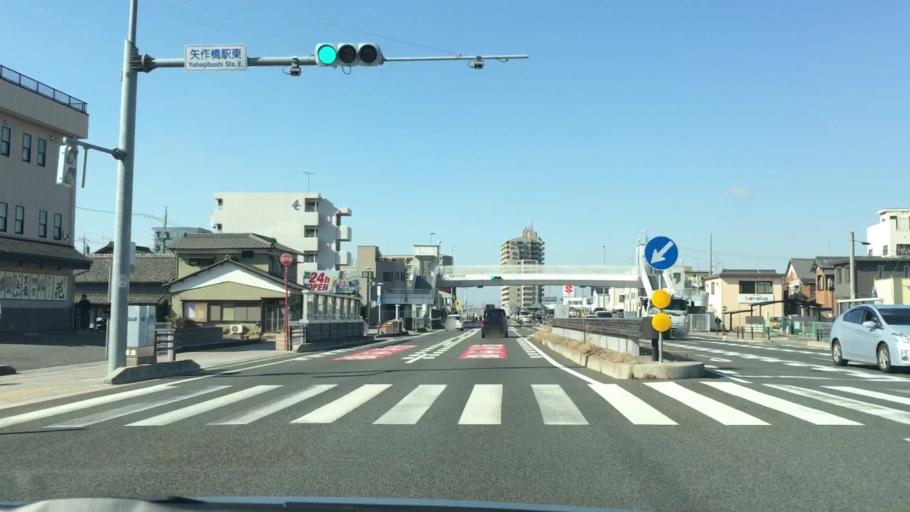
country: JP
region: Aichi
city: Okazaki
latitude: 34.9621
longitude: 137.1424
